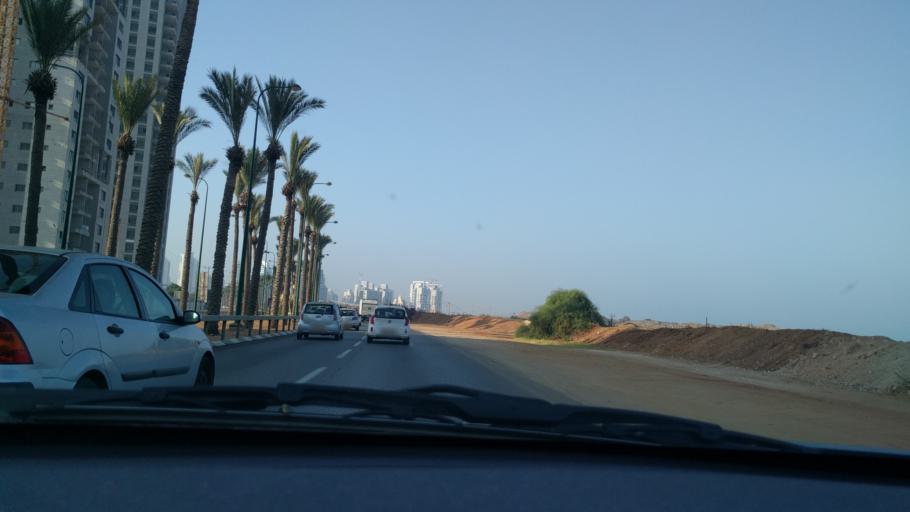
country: IL
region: Central District
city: Netanya
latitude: 32.2940
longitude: 34.8425
